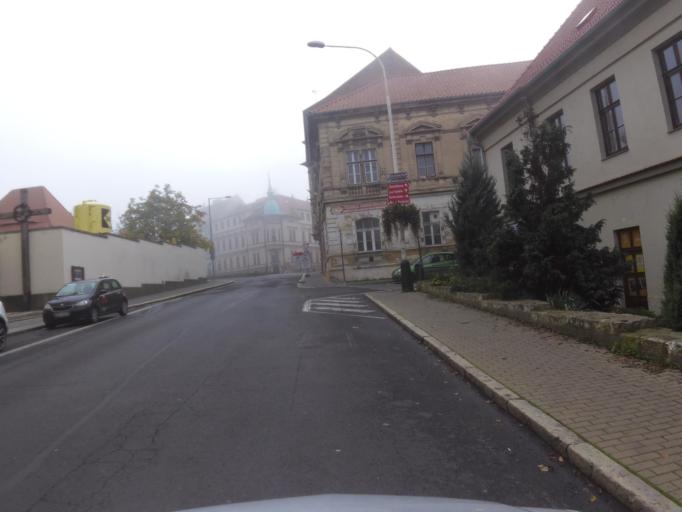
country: CZ
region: Ustecky
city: Zatec
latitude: 50.3252
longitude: 13.5472
